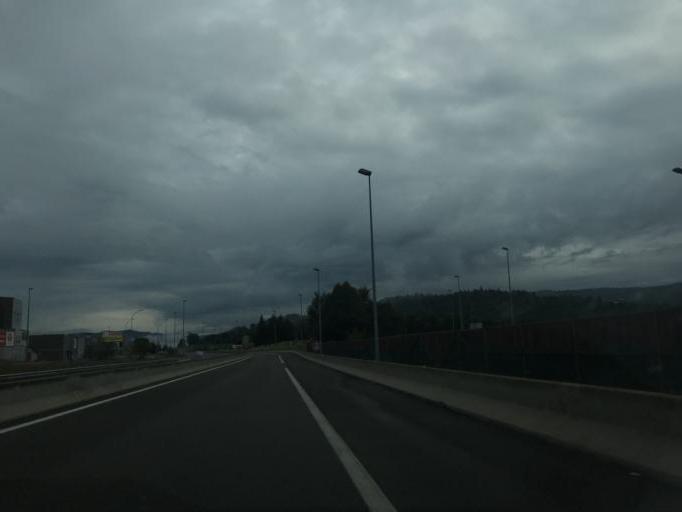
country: FR
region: Rhone-Alpes
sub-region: Departement de l'Ain
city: Arbent
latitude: 46.2826
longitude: 5.6609
